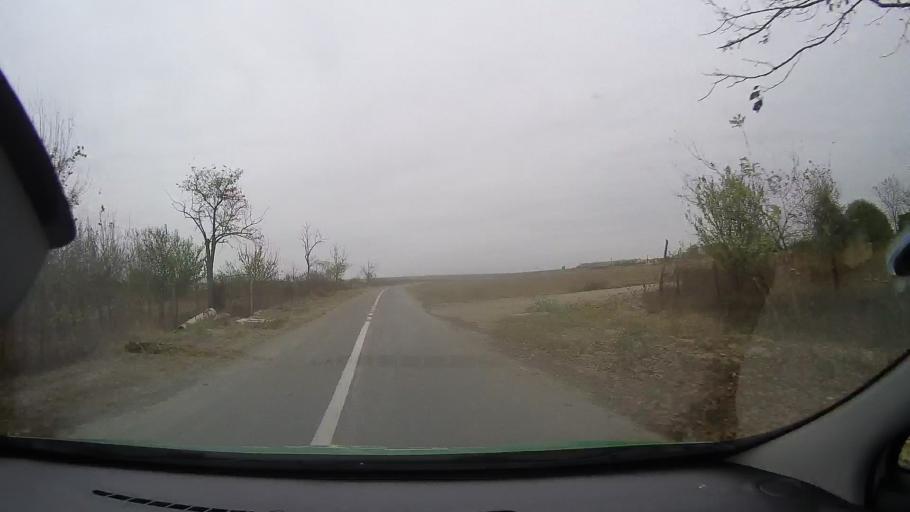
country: RO
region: Constanta
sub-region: Comuna Vulturu
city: Vulturu
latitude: 44.6564
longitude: 28.2667
